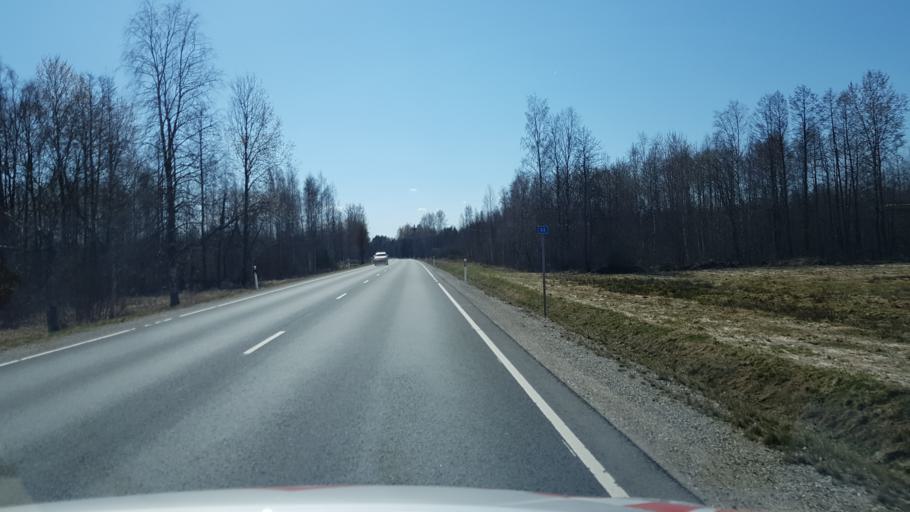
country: EE
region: Jogevamaa
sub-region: Mustvee linn
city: Mustvee
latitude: 58.8837
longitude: 26.9569
